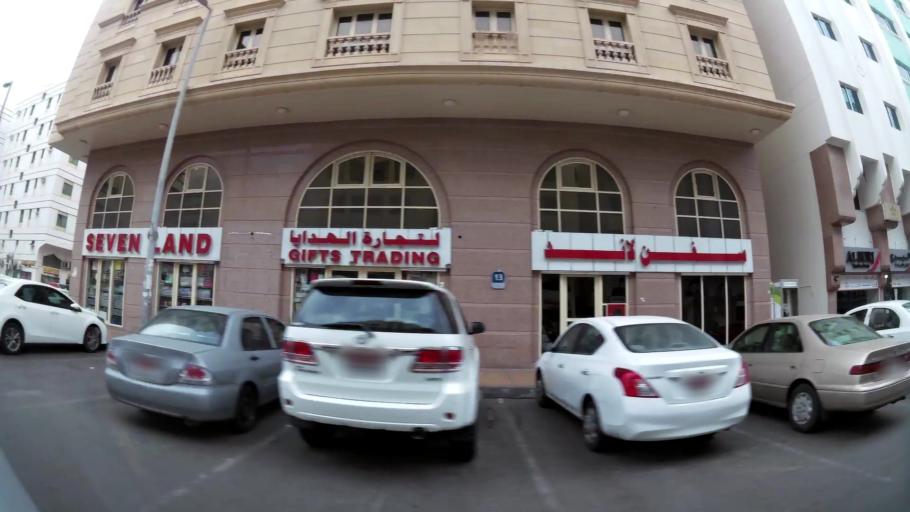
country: AE
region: Abu Dhabi
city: Abu Dhabi
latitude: 24.4811
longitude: 54.3644
